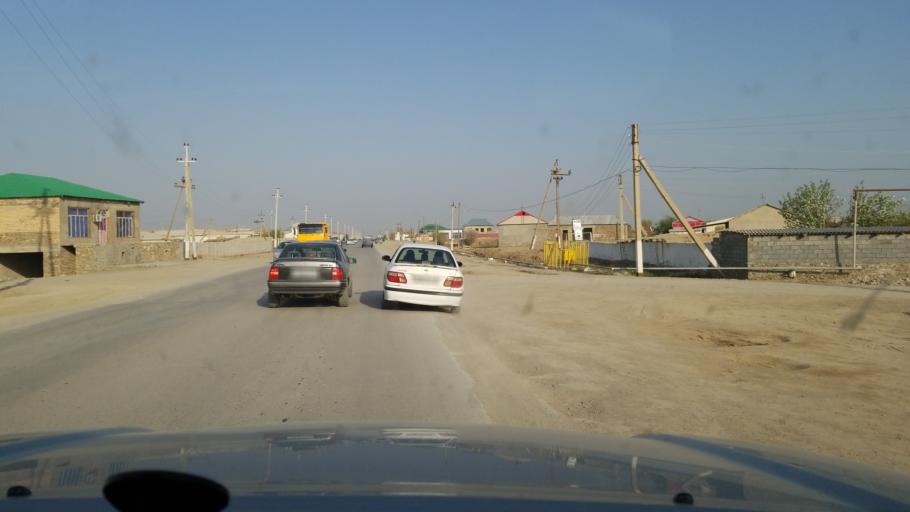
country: AF
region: Jowzjan
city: Qarqin
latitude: 37.5164
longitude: 66.0200
